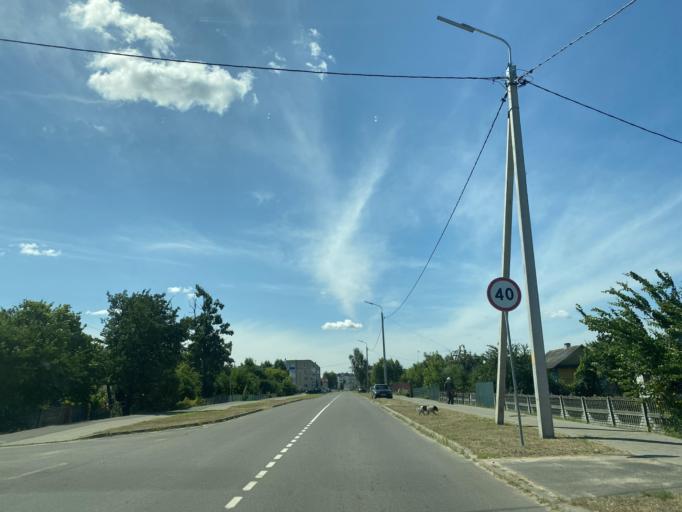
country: BY
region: Brest
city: Ivanava
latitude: 52.1539
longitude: 25.5437
